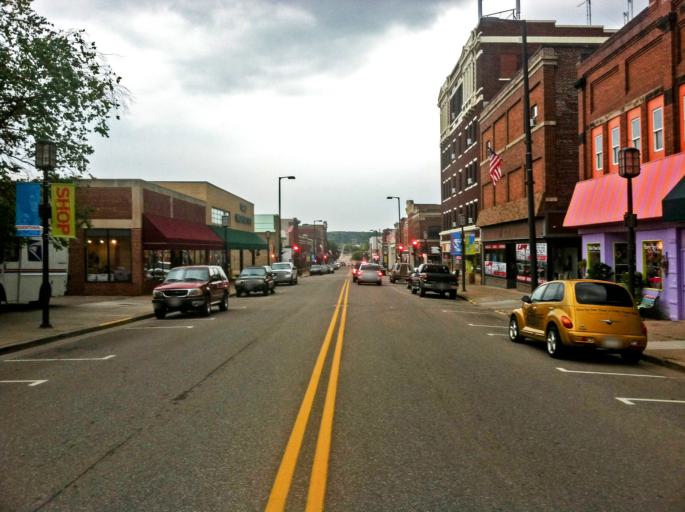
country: US
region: Wisconsin
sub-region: Chippewa County
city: Chippewa Falls
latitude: 44.9376
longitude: -91.3939
